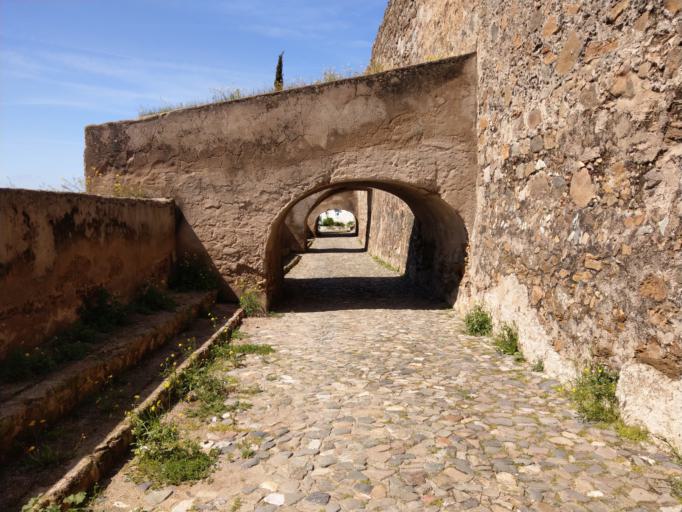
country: PT
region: Portalegre
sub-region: Campo Maior
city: Campo Maior
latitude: 39.0107
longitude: -7.0724
